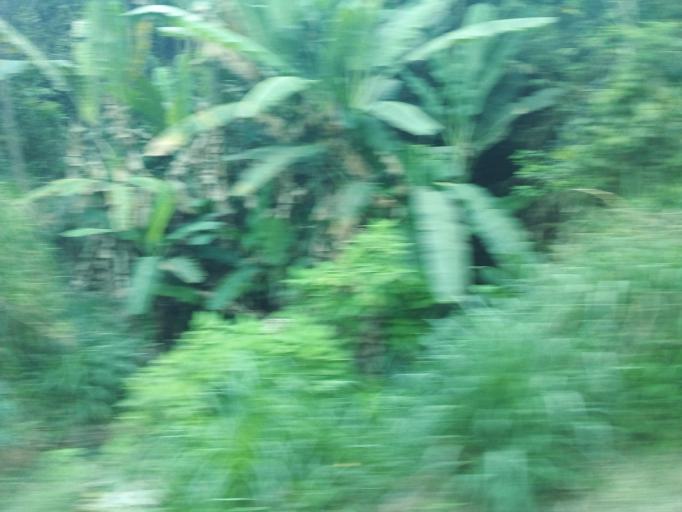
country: BR
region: Minas Gerais
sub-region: Nova Era
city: Nova Era
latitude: -19.7317
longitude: -43.0165
